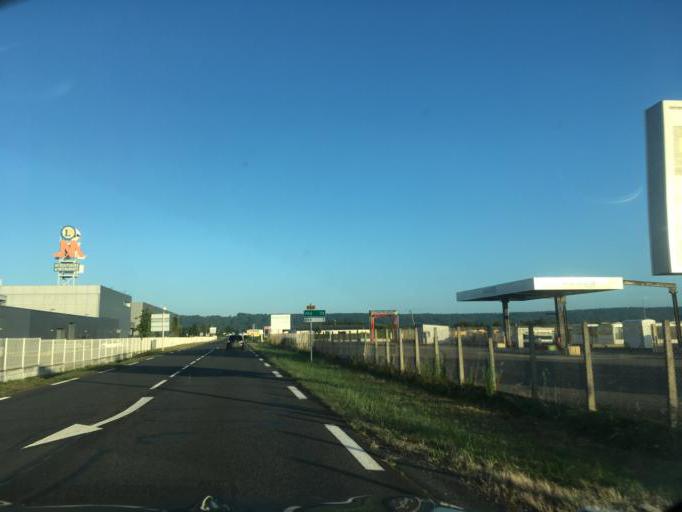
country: FR
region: Midi-Pyrenees
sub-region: Departement des Hautes-Pyrenees
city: Ibos
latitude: 43.2407
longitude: 0.0155
